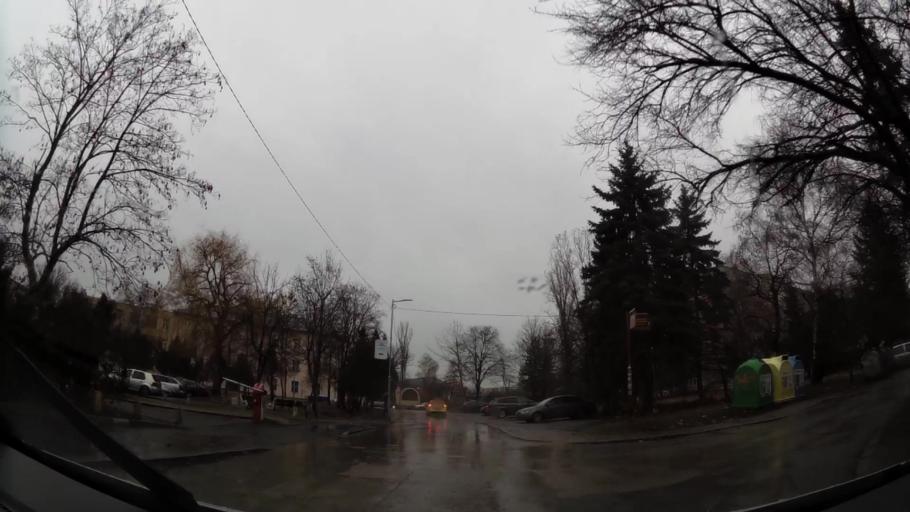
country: BG
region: Sofia-Capital
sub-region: Stolichna Obshtina
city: Sofia
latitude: 42.6590
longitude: 23.3511
